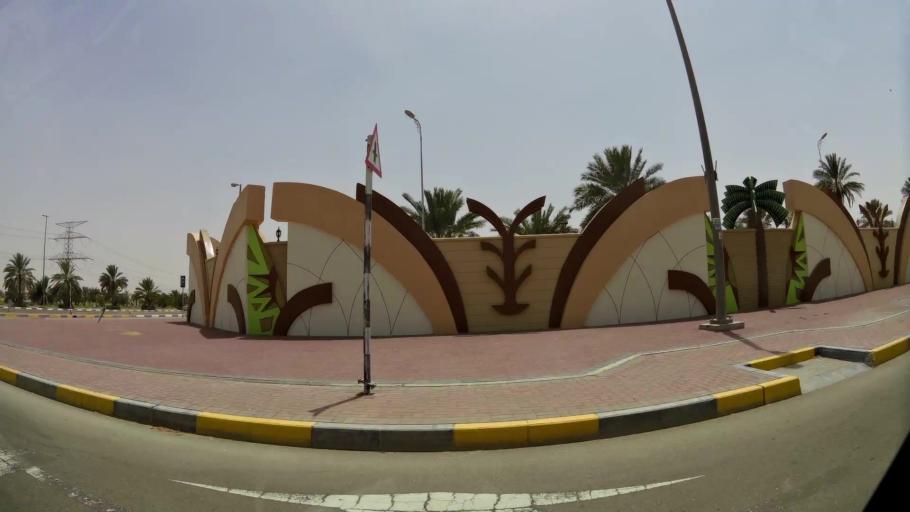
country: AE
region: Abu Dhabi
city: Al Ain
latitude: 24.1842
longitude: 55.6765
